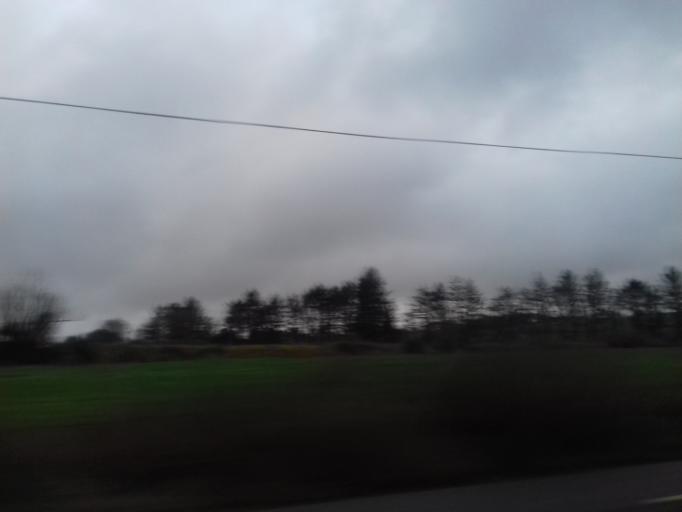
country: IE
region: Munster
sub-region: Ciarrai
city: Castleisland
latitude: 52.3019
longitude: -9.3822
